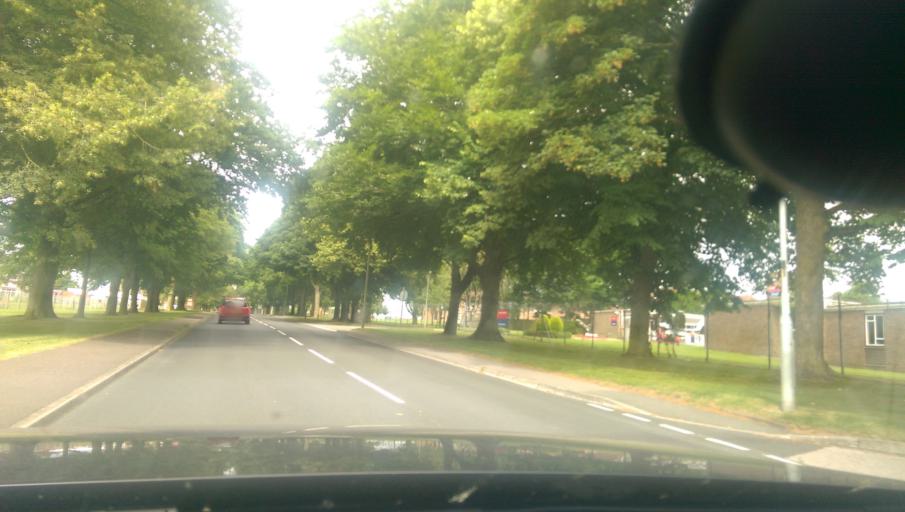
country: GB
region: England
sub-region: Wiltshire
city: Amesbury
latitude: 51.1975
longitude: -1.8168
